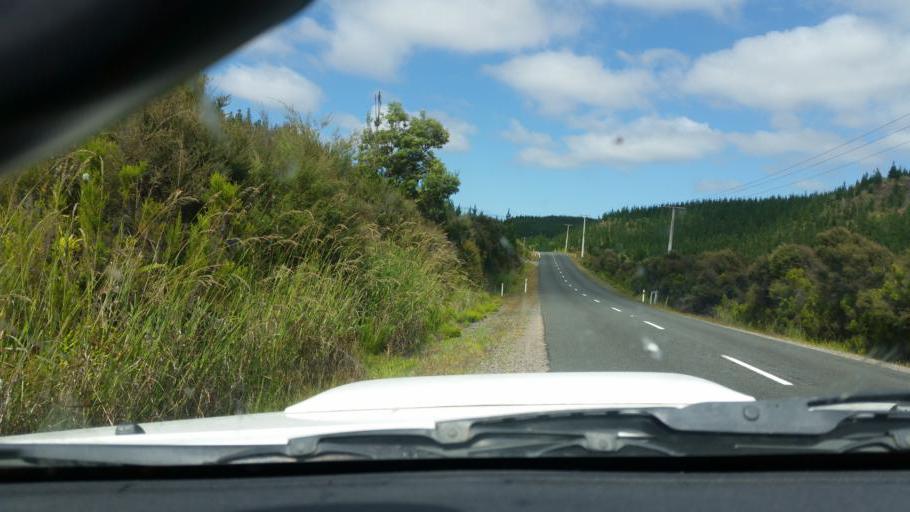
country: NZ
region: Northland
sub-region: Kaipara District
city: Dargaville
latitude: -35.8170
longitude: 173.7145
